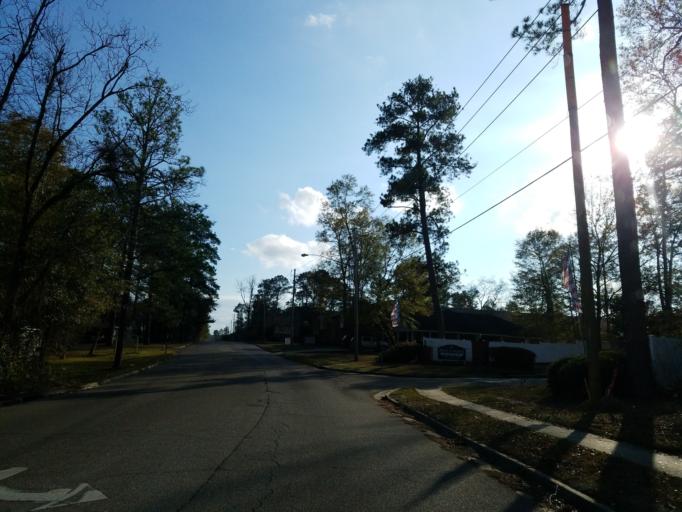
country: US
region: Mississippi
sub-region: Lamar County
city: Arnold Line
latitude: 31.3343
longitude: -89.3455
